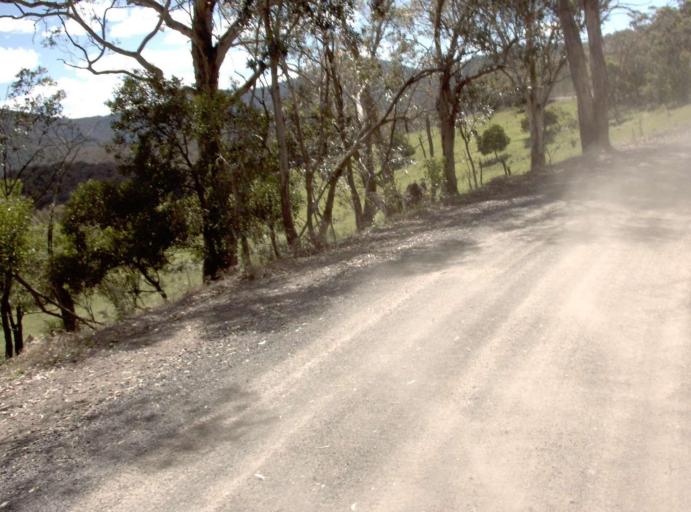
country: AU
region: New South Wales
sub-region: Bombala
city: Bombala
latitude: -37.1494
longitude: 148.6667
